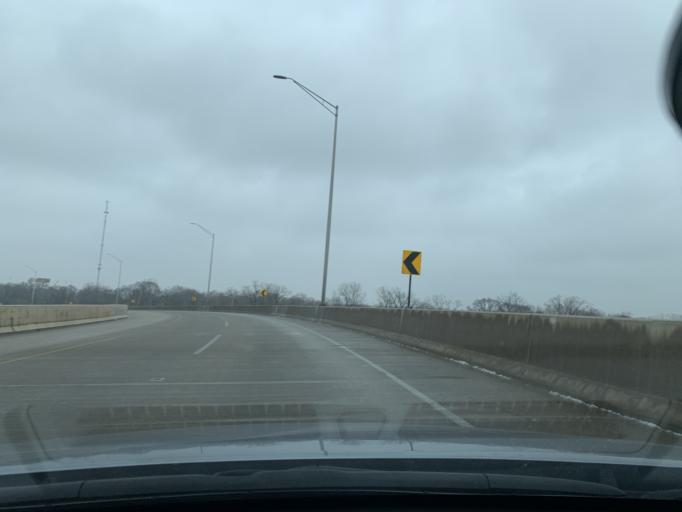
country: US
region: Illinois
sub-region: Cook County
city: Posen
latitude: 41.6155
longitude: -87.6873
